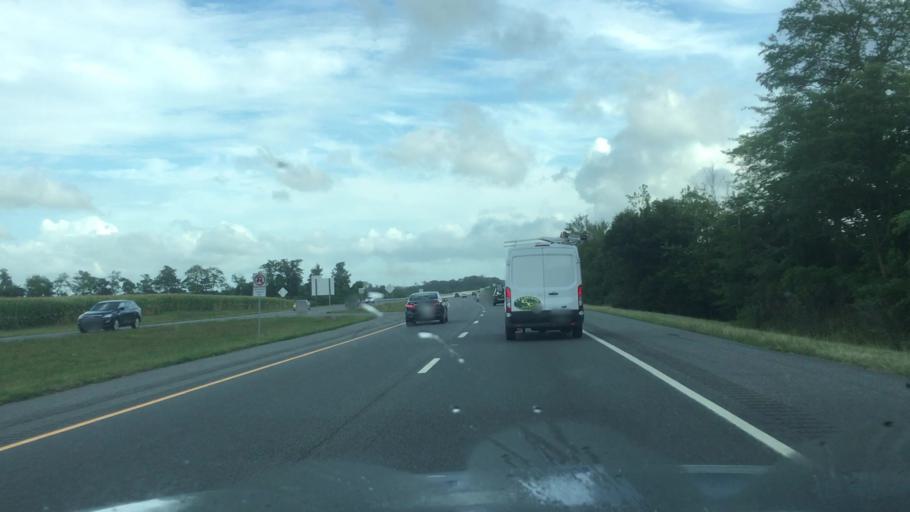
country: US
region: Delaware
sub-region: Kent County
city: Dover Base Housing
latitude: 39.0961
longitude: -75.4555
